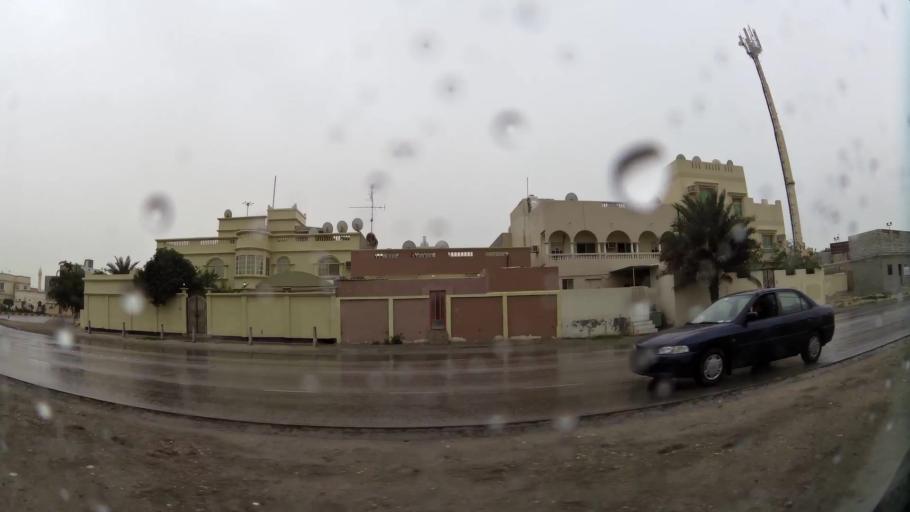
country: BH
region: Northern
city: Madinat `Isa
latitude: 26.1601
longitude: 50.5701
